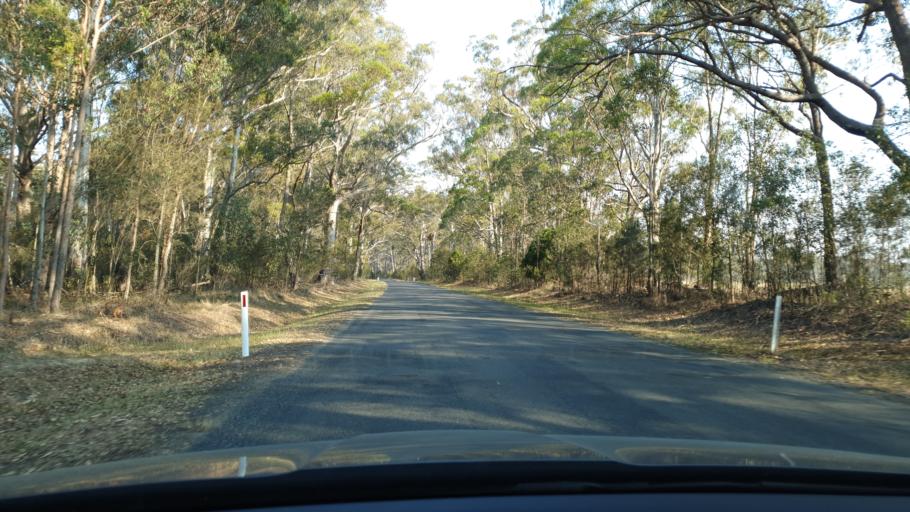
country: AU
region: New South Wales
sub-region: Tenterfield Municipality
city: Carrolls Creek
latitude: -28.6969
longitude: 152.0925
